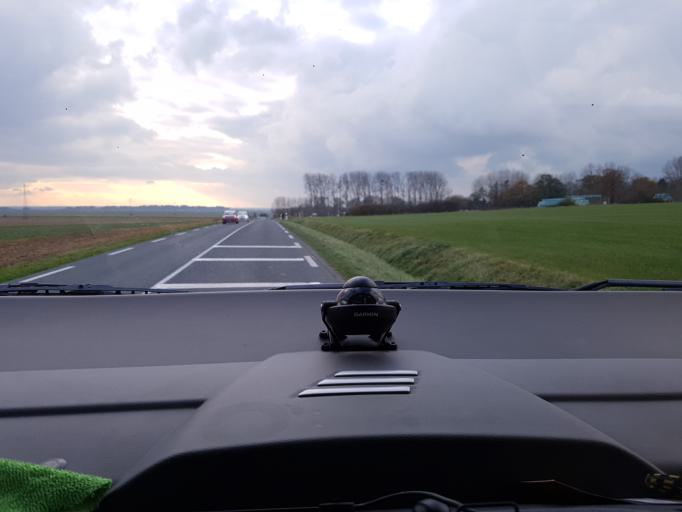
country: FR
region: Haute-Normandie
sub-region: Departement de la Seine-Maritime
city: Hautot-sur-Mer
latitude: 49.8927
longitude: 1.0413
